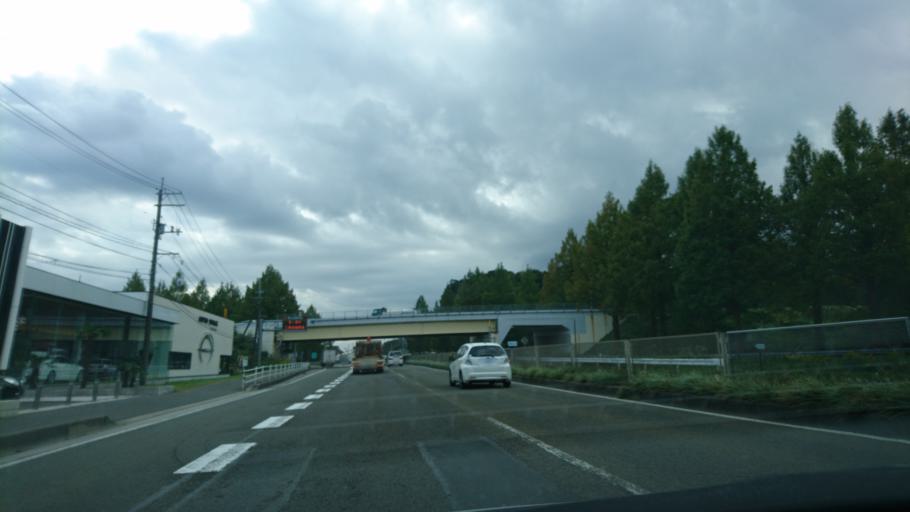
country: JP
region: Miyagi
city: Tomiya
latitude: 38.3451
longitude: 140.8790
